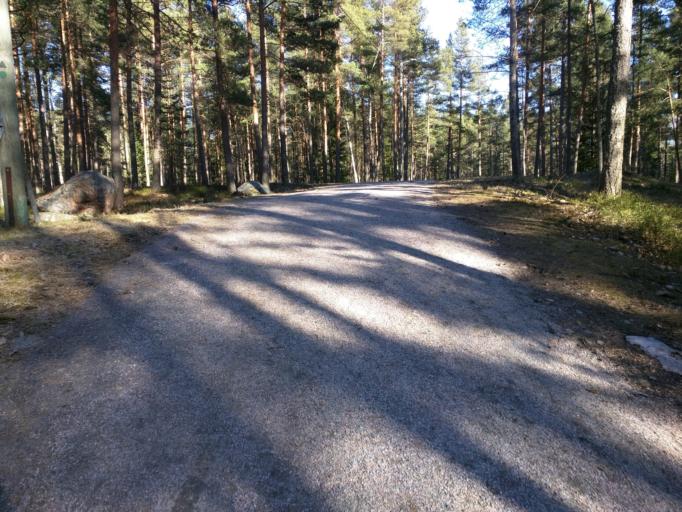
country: FI
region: Uusimaa
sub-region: Helsinki
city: Kilo
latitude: 60.2313
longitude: 24.7877
